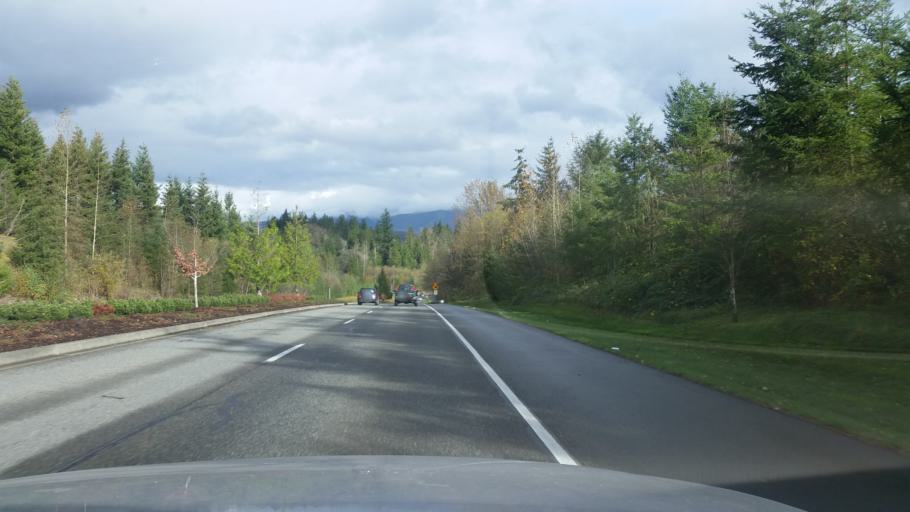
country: US
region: Washington
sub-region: King County
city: Snoqualmie
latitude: 47.5334
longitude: -121.8490
